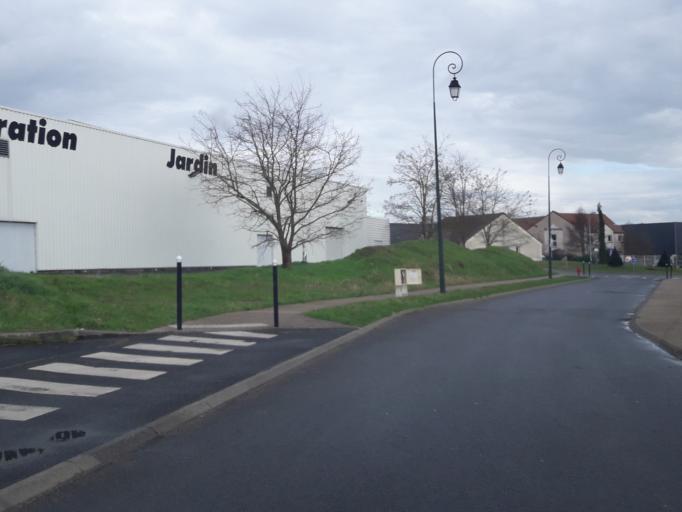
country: FR
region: Ile-de-France
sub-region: Departement de l'Essonne
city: Ballancourt-sur-Essonne
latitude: 48.5288
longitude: 2.3883
